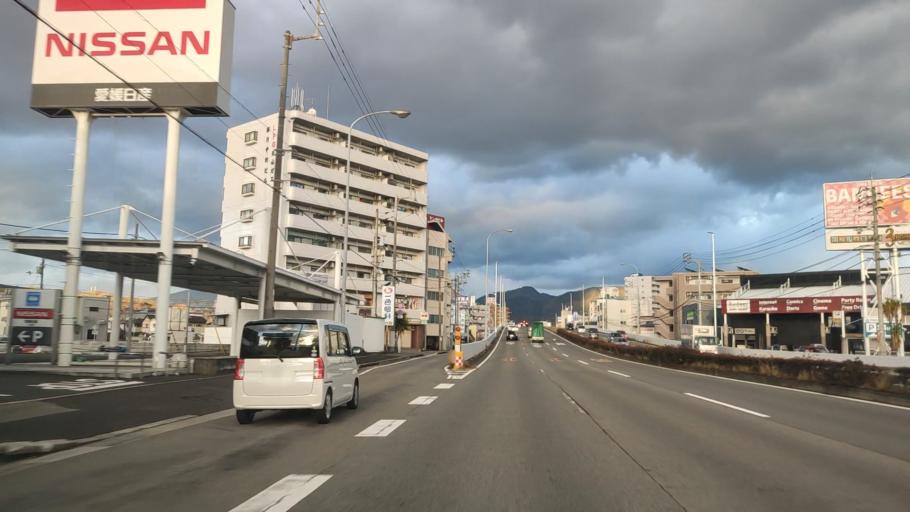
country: JP
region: Ehime
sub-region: Shikoku-chuo Shi
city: Matsuyama
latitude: 33.8239
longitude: 132.7791
